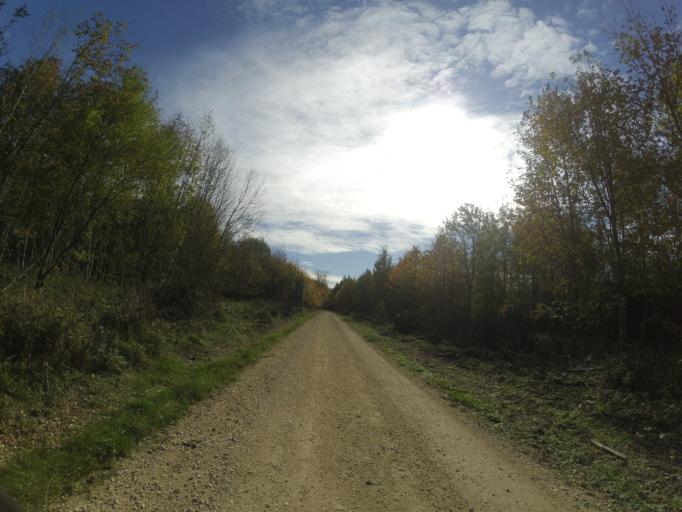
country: DE
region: Baden-Wuerttemberg
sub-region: Tuebingen Region
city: Lonsee
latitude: 48.5953
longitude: 9.9461
